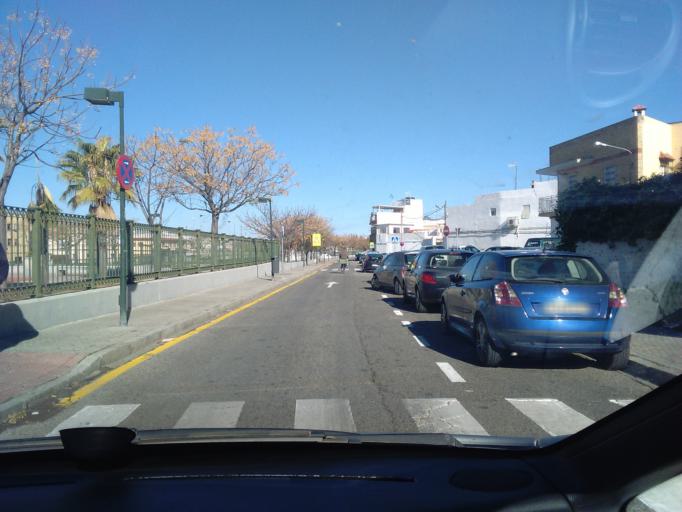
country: ES
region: Andalusia
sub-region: Provincia de Sevilla
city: Sevilla
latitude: 37.3864
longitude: -5.9091
